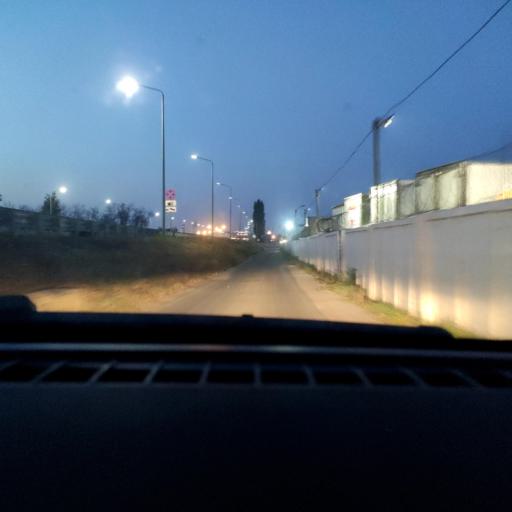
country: RU
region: Voronezj
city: Somovo
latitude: 51.6756
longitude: 39.3006
